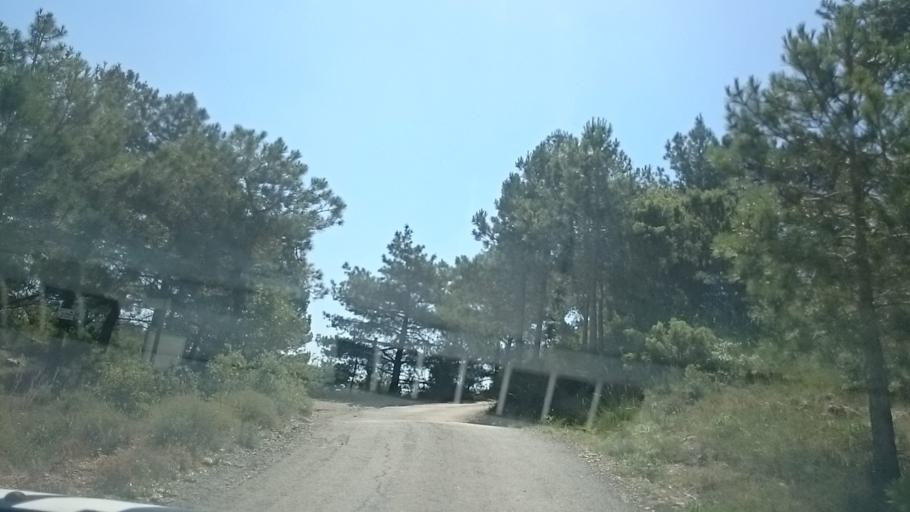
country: ES
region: Catalonia
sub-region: Provincia de Tarragona
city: Querol
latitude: 41.4105
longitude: 1.4244
